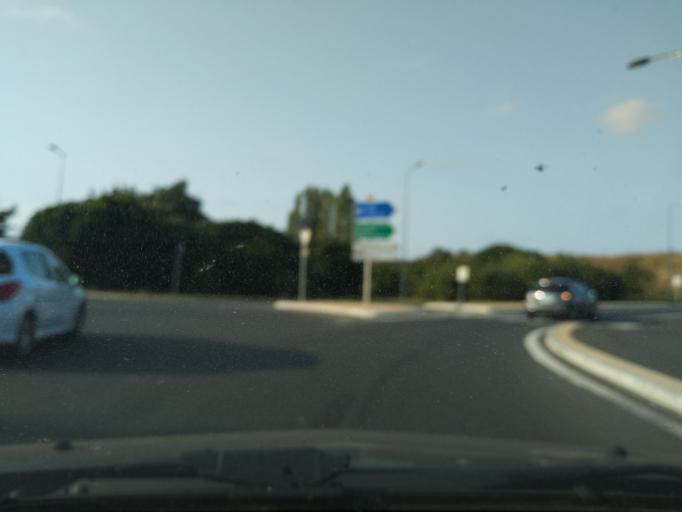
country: FR
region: Centre
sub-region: Departement d'Indre-et-Loire
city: La Membrolle-sur-Choisille
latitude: 47.4292
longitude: 0.6507
